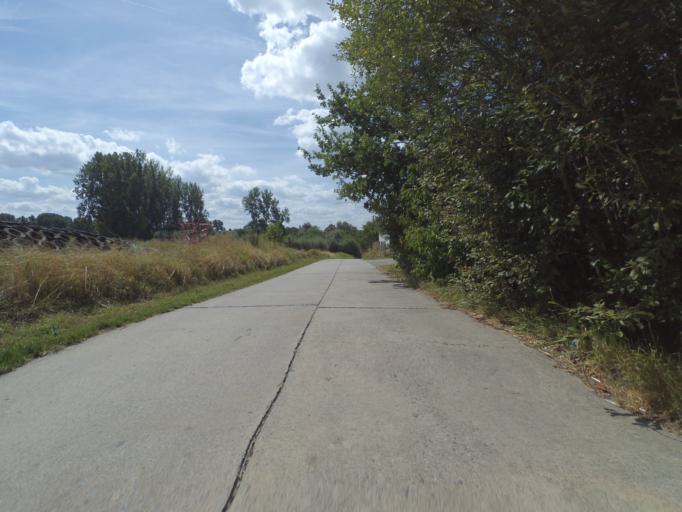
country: BE
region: Flanders
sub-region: Provincie Oost-Vlaanderen
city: Zottegem
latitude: 50.8601
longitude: 3.7810
